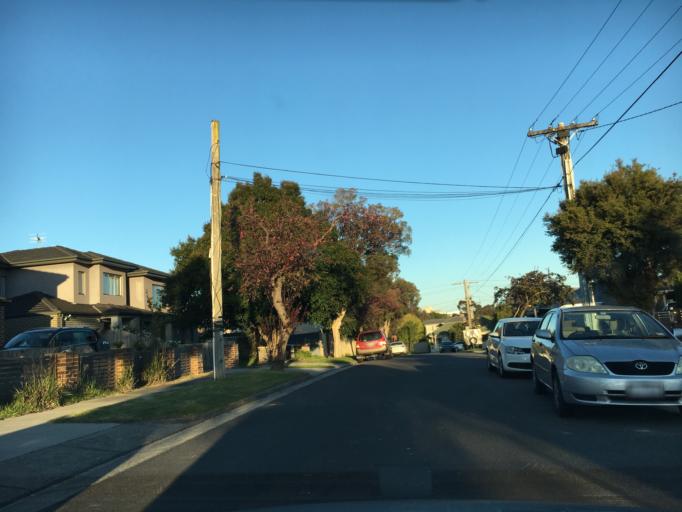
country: AU
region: Victoria
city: Clayton
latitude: -37.9103
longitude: 145.1145
